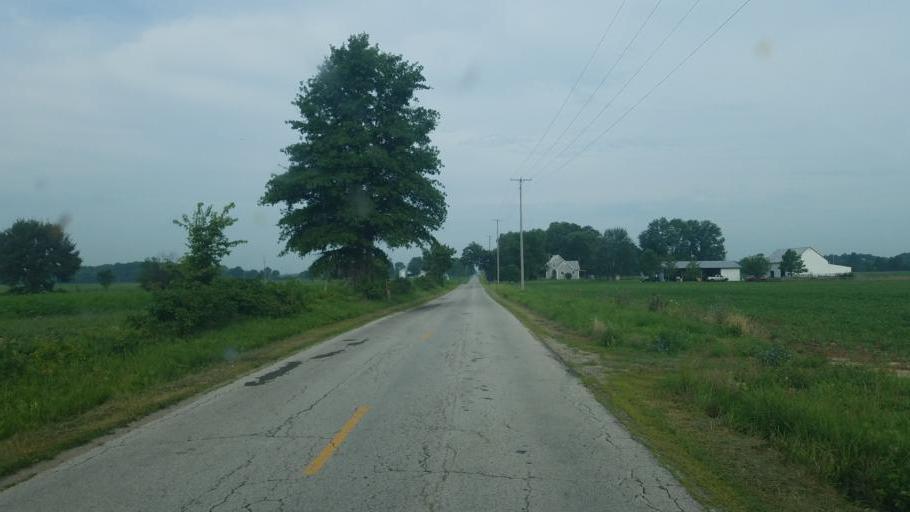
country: US
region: Ohio
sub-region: Morrow County
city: Cardington
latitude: 40.4677
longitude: -82.9076
